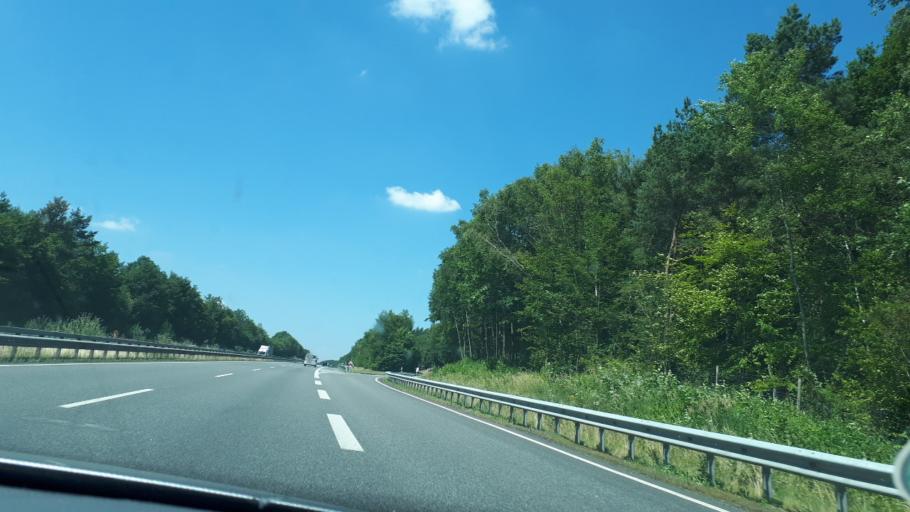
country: DE
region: Rheinland-Pfalz
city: Wolken
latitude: 50.3409
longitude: 7.4483
